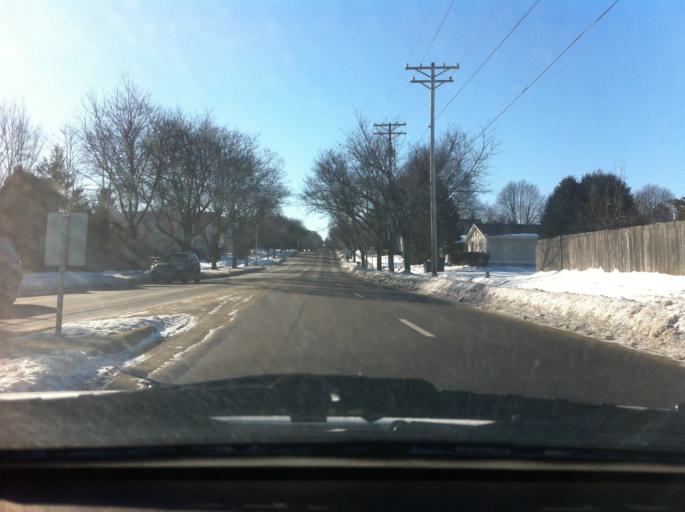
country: US
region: Wisconsin
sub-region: Dane County
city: Middleton
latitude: 43.0812
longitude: -89.5023
